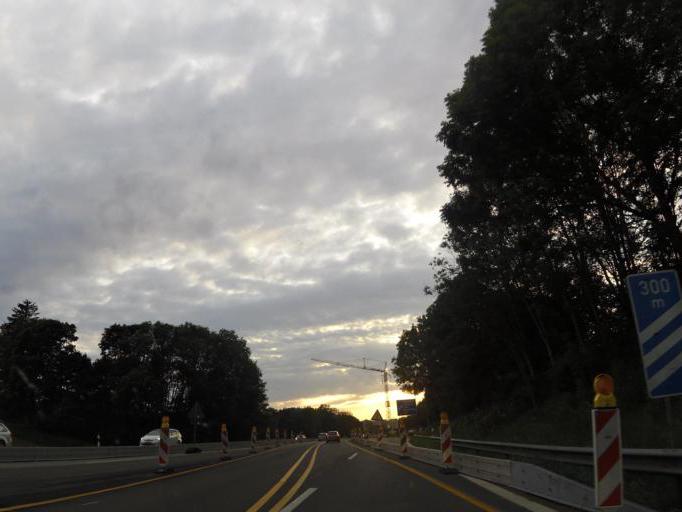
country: DE
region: Bavaria
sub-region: Upper Bavaria
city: Siegsdorf
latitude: 47.8259
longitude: 12.6516
